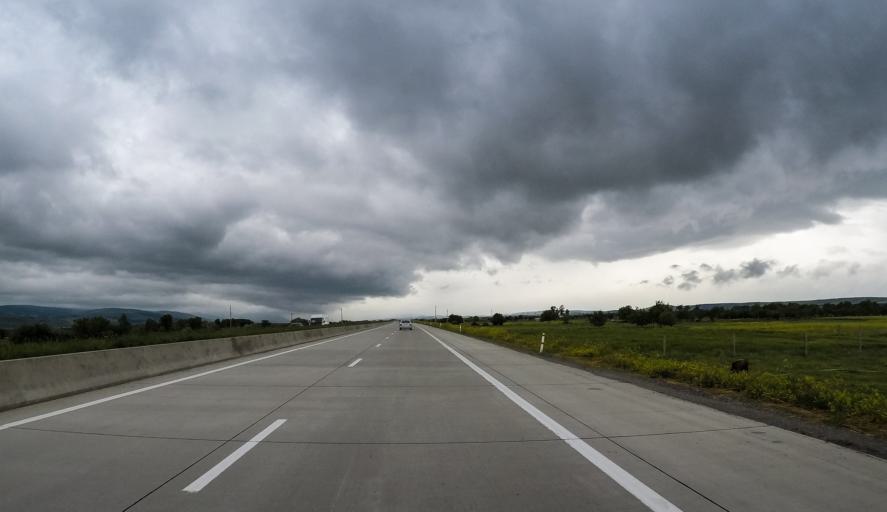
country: GE
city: Agara
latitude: 42.0282
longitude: 43.8202
